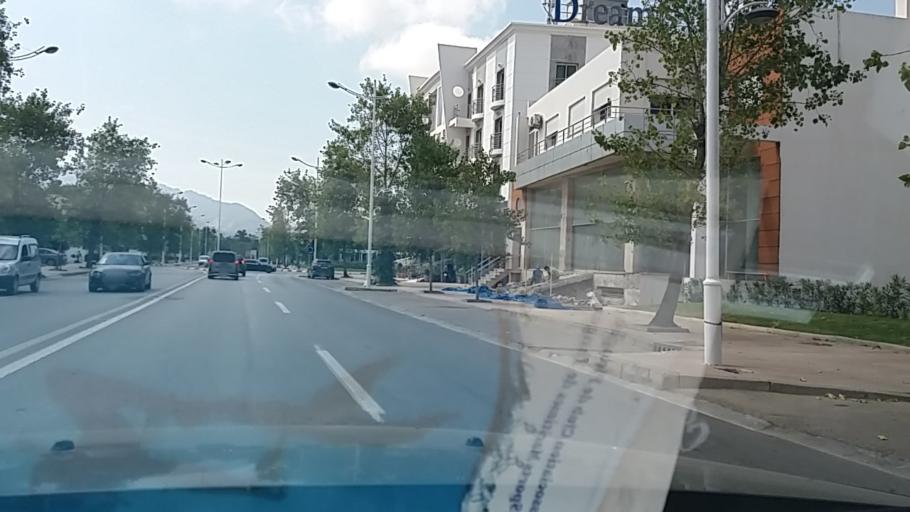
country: MA
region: Tanger-Tetouan
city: Tetouan
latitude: 35.5821
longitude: -5.3344
